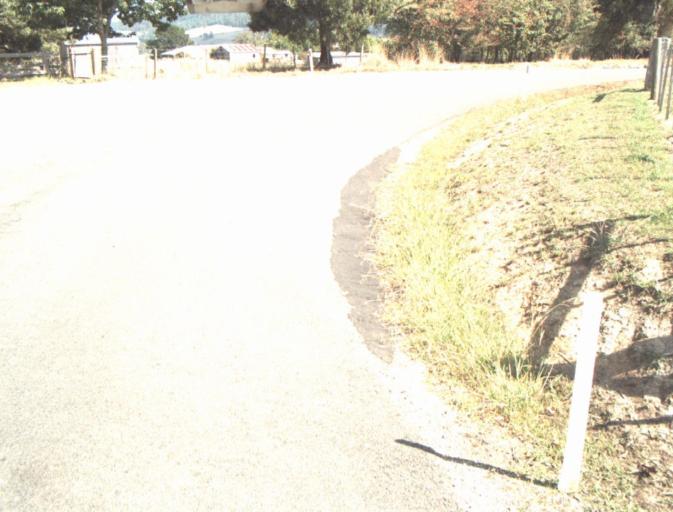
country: AU
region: Tasmania
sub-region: Launceston
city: Mayfield
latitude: -41.2407
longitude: 147.2331
